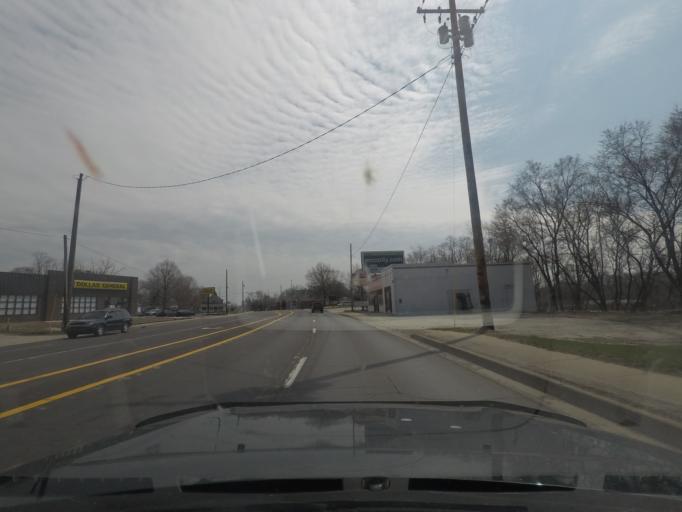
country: US
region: Indiana
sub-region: LaPorte County
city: LaPorte
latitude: 41.6210
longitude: -86.7380
